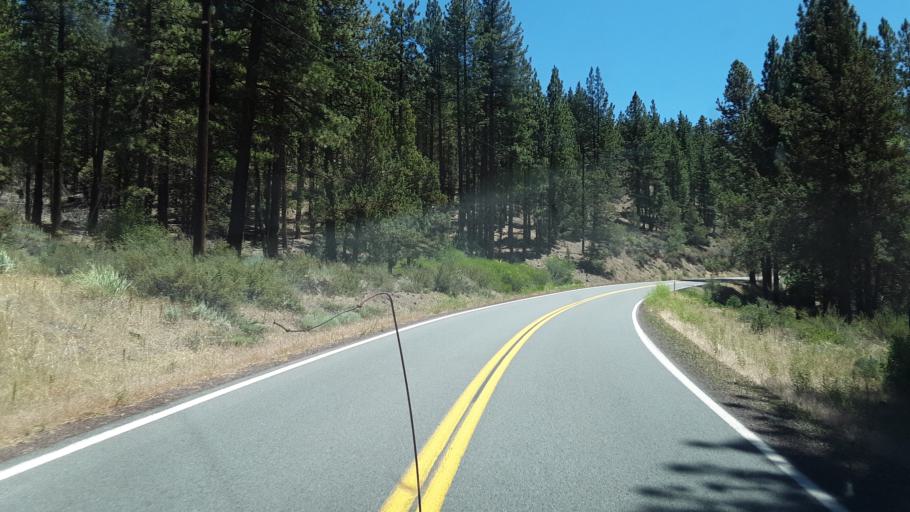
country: US
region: California
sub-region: Modoc County
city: Alturas
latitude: 41.0338
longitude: -120.8547
